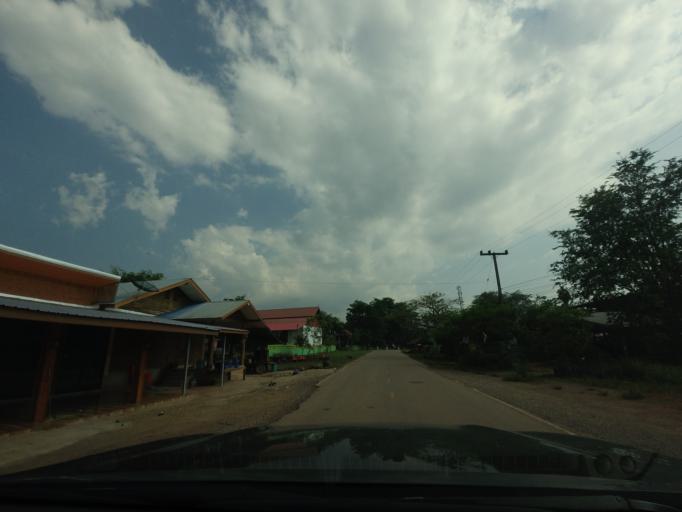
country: TH
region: Phitsanulok
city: Nakhon Thai
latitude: 17.0499
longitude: 100.9091
